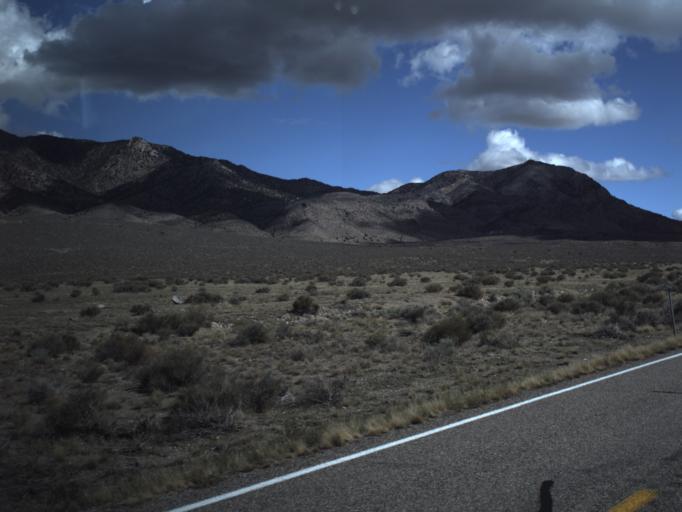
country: US
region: Utah
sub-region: Beaver County
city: Milford
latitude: 38.4451
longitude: -113.3292
